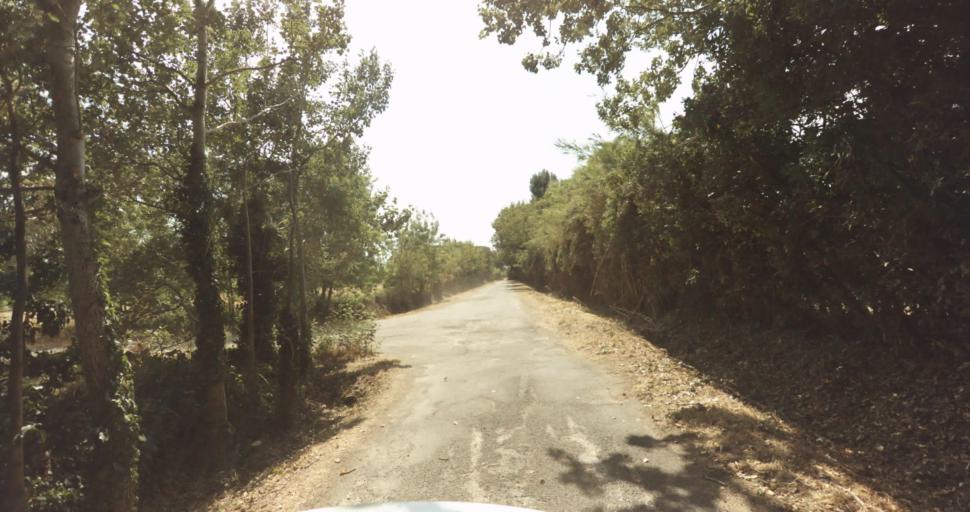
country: FR
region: Languedoc-Roussillon
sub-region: Departement des Pyrenees-Orientales
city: Latour-Bas-Elne
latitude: 42.6042
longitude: 3.0286
